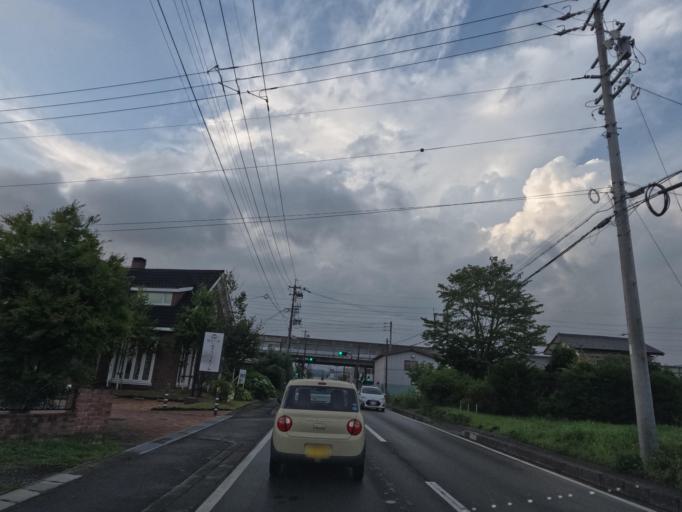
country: JP
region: Nagano
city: Komoro
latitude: 36.3406
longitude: 138.5922
